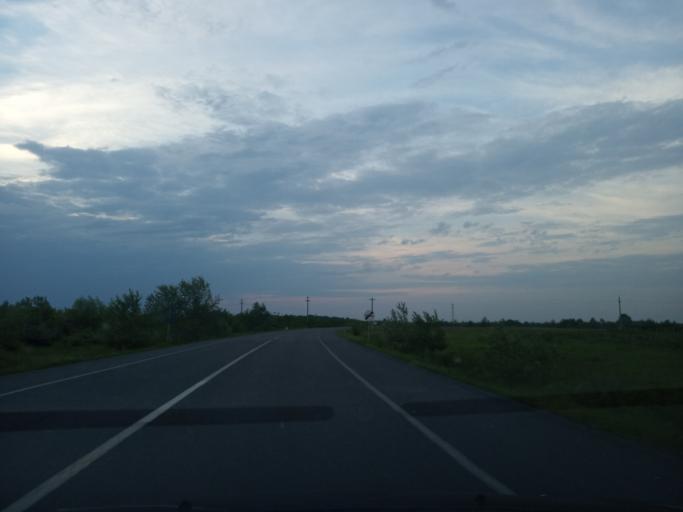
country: RO
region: Timis
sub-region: Oras Deta
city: Deta
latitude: 45.3754
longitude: 21.2337
